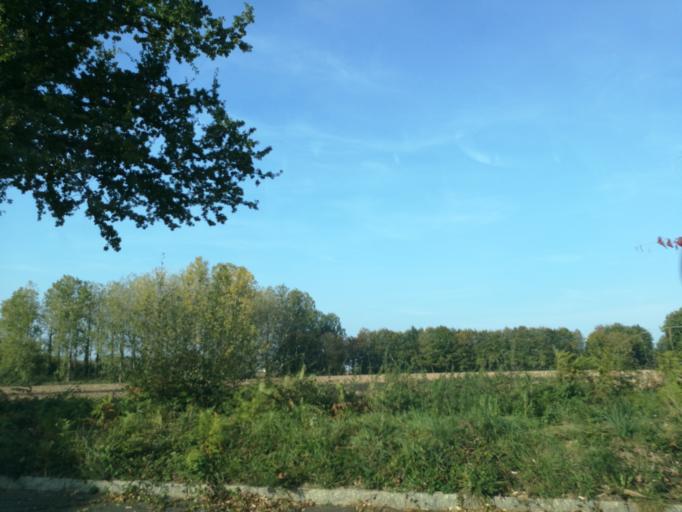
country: FR
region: Brittany
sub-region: Departement d'Ille-et-Vilaine
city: Breteil
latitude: 48.1495
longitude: -1.9018
